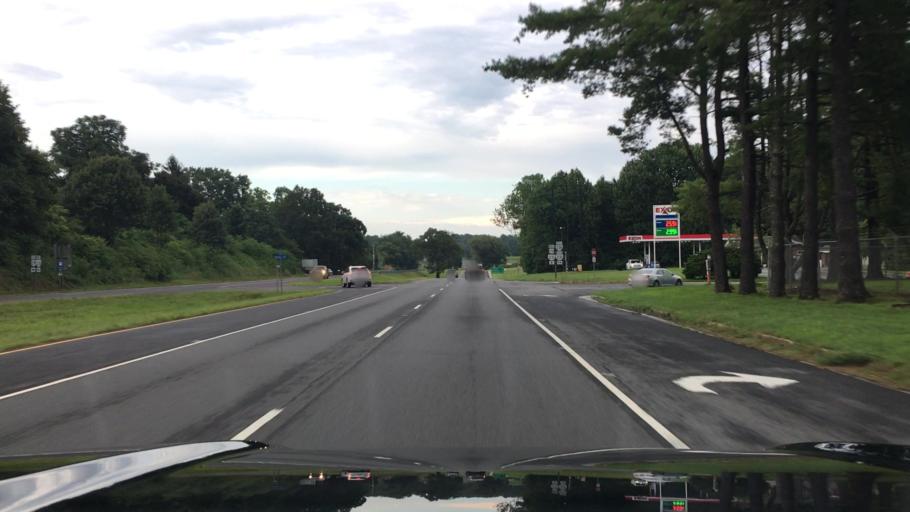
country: US
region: Virginia
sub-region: Madison County
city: Madison
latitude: 38.3526
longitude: -78.2797
